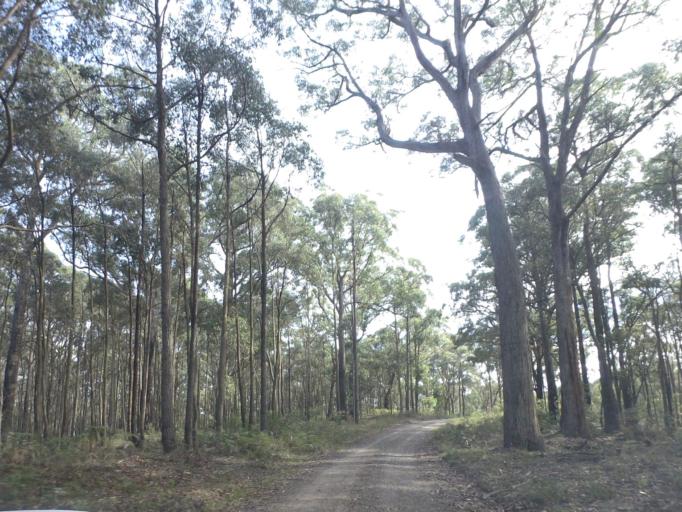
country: AU
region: Victoria
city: Brown Hill
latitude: -37.4873
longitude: 144.1951
